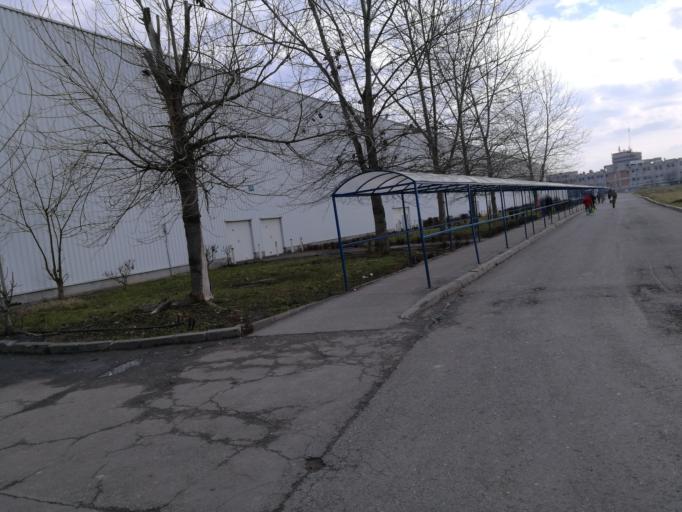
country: RO
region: Ilfov
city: Dobroesti
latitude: 44.4377
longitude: 26.1848
